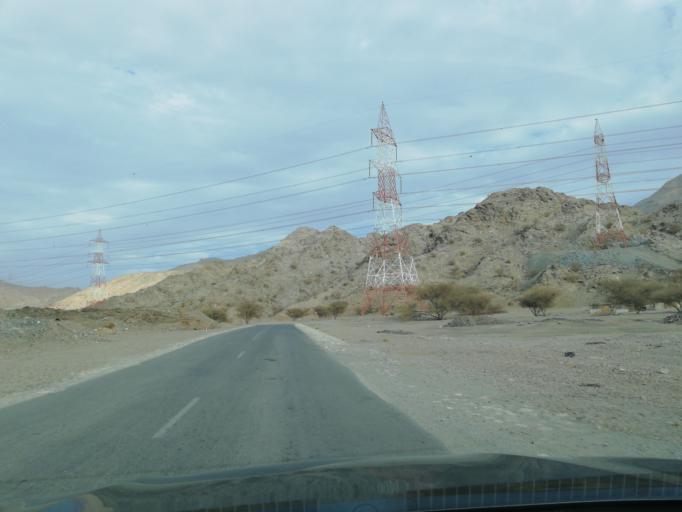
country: OM
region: Muhafazat Masqat
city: Bawshar
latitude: 23.4708
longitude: 58.3121
